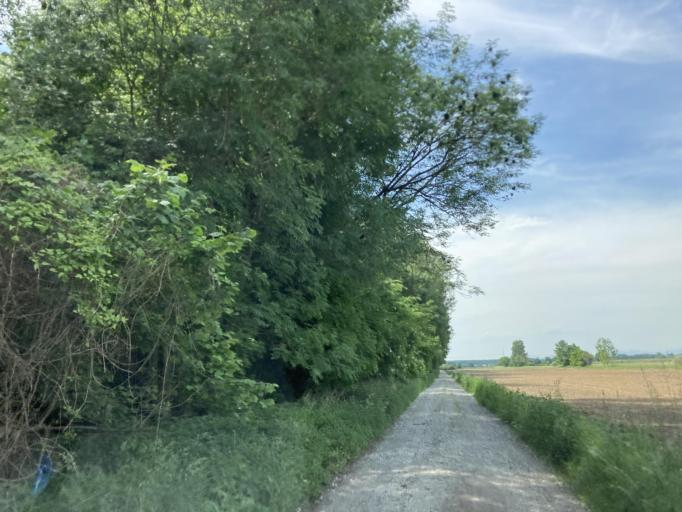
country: DE
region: Baden-Wuerttemberg
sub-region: Karlsruhe Region
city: Graben-Neudorf
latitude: 49.1733
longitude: 8.4620
